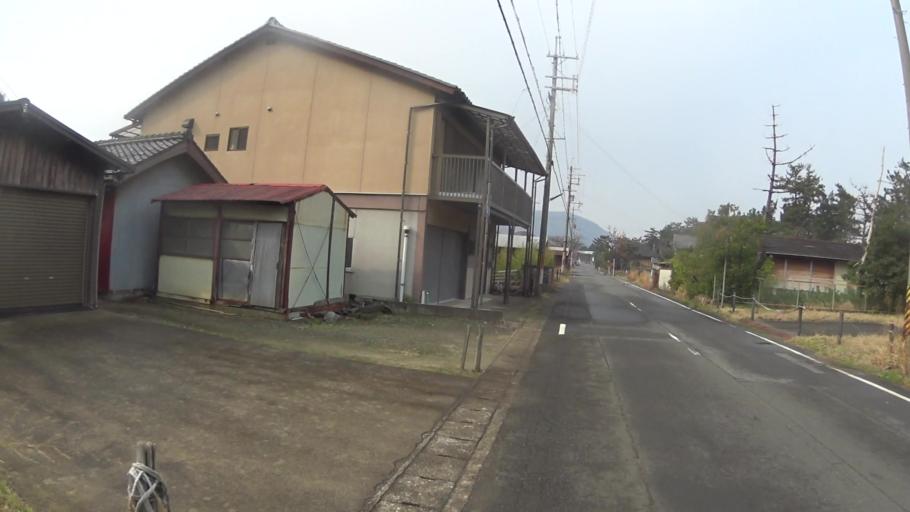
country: JP
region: Kyoto
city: Maizuru
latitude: 35.5126
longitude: 135.3030
